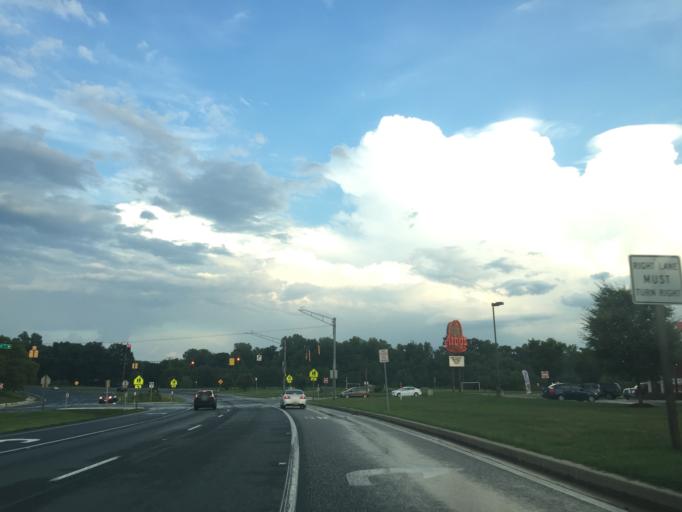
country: US
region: Maryland
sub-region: Harford County
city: Riverside
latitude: 39.4785
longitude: -76.2485
